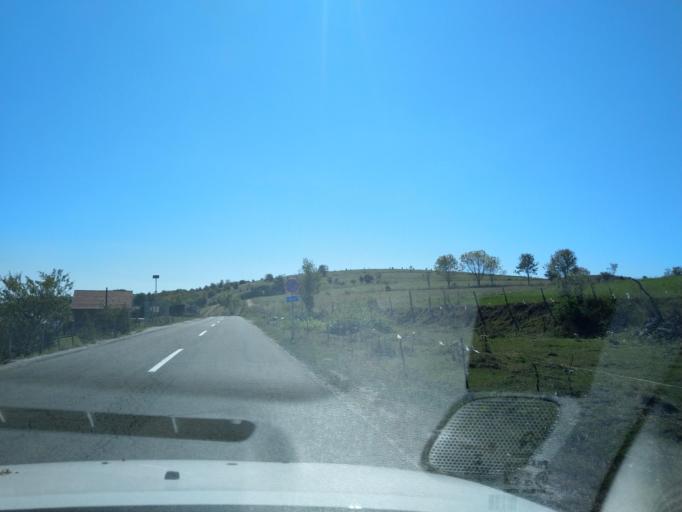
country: RS
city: Sokolovica
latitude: 43.2714
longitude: 20.2236
